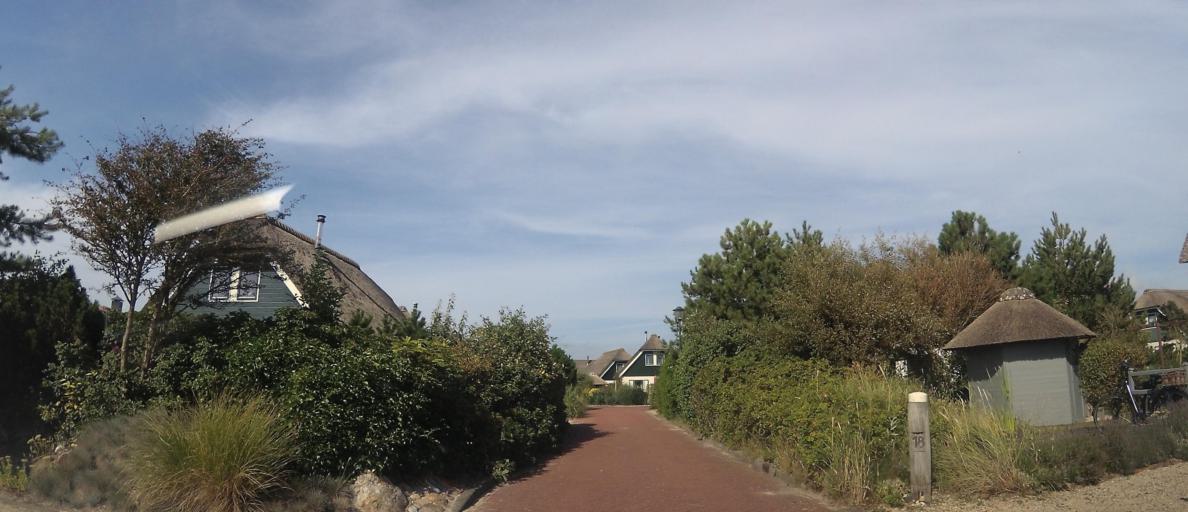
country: NL
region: North Holland
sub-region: Gemeente Den Helder
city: Den Helder
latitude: 52.9066
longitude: 4.7231
